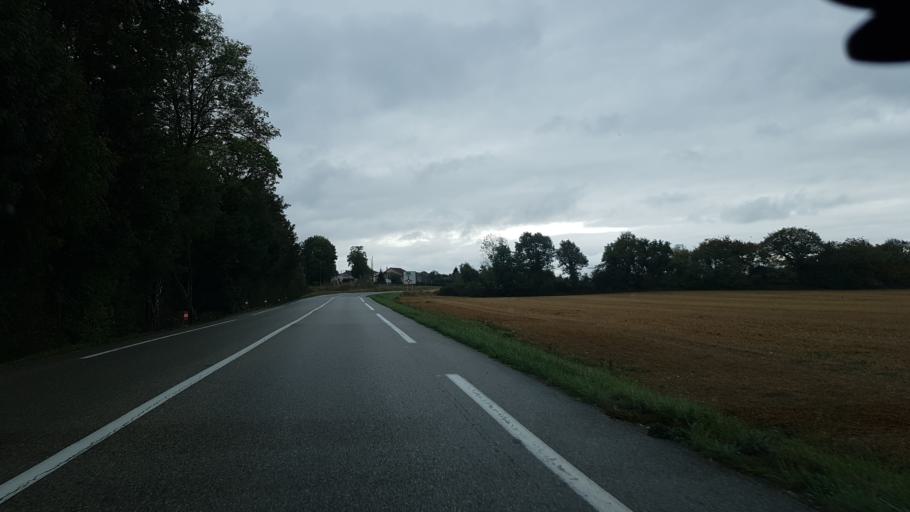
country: FR
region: Rhone-Alpes
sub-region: Departement de l'Ain
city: Ambronay
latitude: 45.9989
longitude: 5.3422
